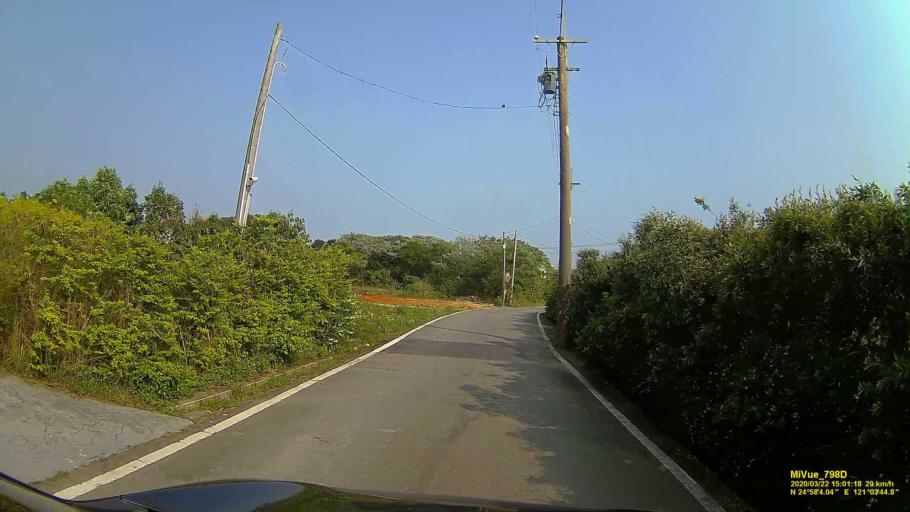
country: TW
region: Taiwan
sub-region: Hsinchu
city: Zhubei
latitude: 24.9677
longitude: 121.0627
